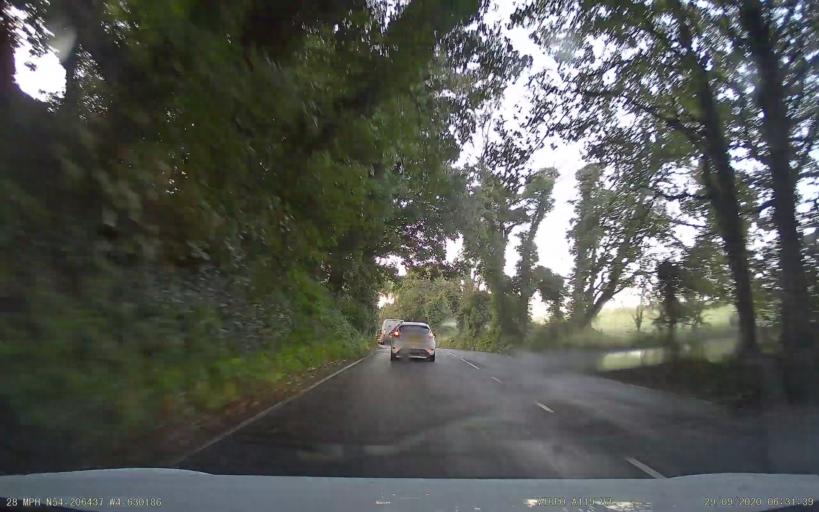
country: IM
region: Castletown
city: Castletown
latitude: 54.2064
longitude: -4.6302
